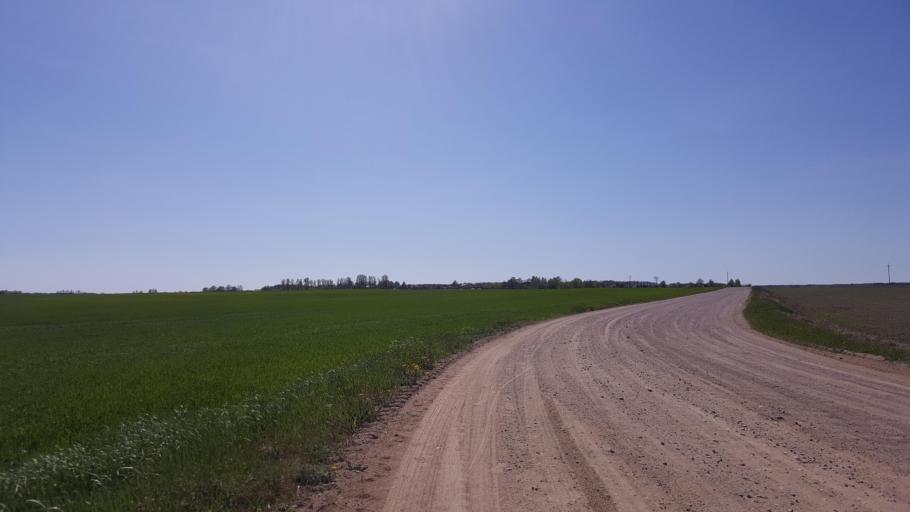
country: BY
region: Brest
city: Kamyanyets
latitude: 52.4466
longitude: 23.8637
